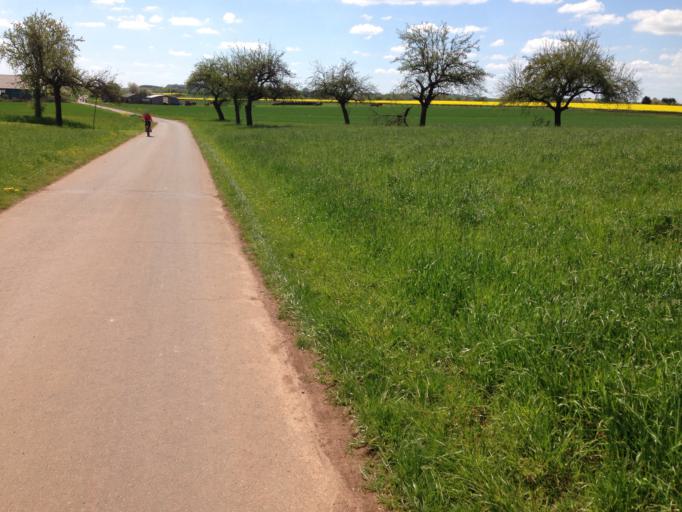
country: DE
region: Hesse
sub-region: Regierungsbezirk Giessen
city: Lich
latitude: 50.5042
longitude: 8.8523
